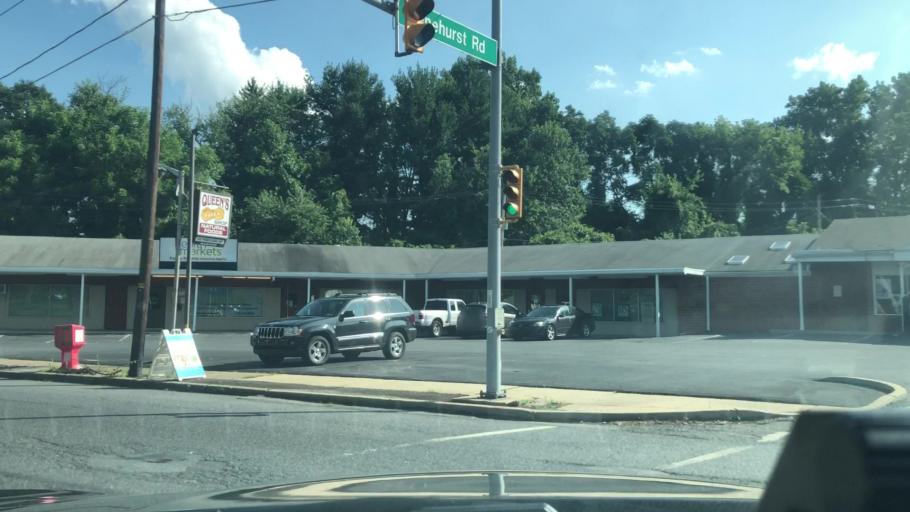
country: US
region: Pennsylvania
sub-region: Lehigh County
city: Fountain Hill
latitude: 40.6355
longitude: -75.4232
